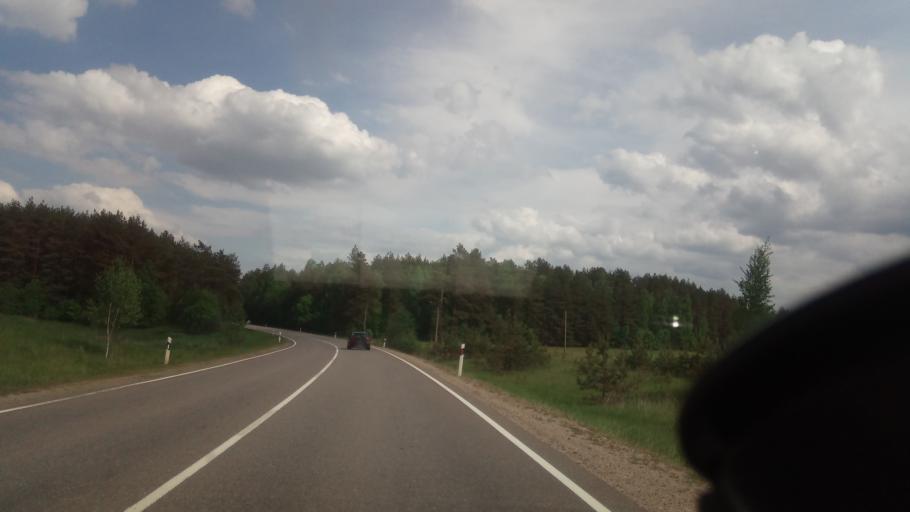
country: LT
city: Trakai
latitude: 54.6068
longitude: 24.8499
